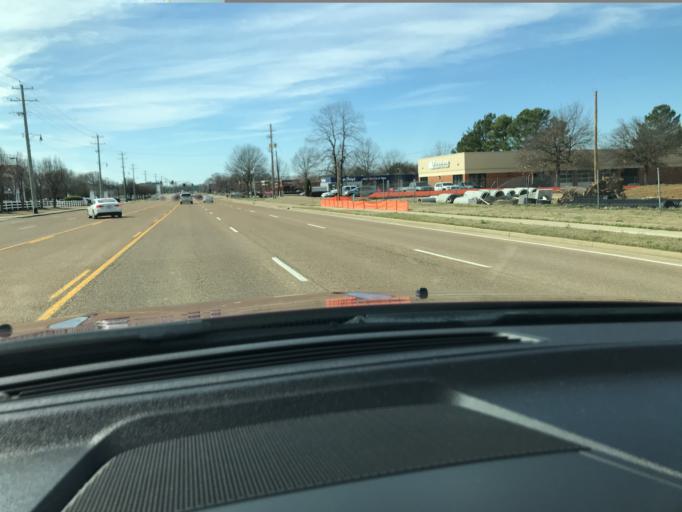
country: US
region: Tennessee
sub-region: Shelby County
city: Collierville
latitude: 35.0464
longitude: -89.6979
